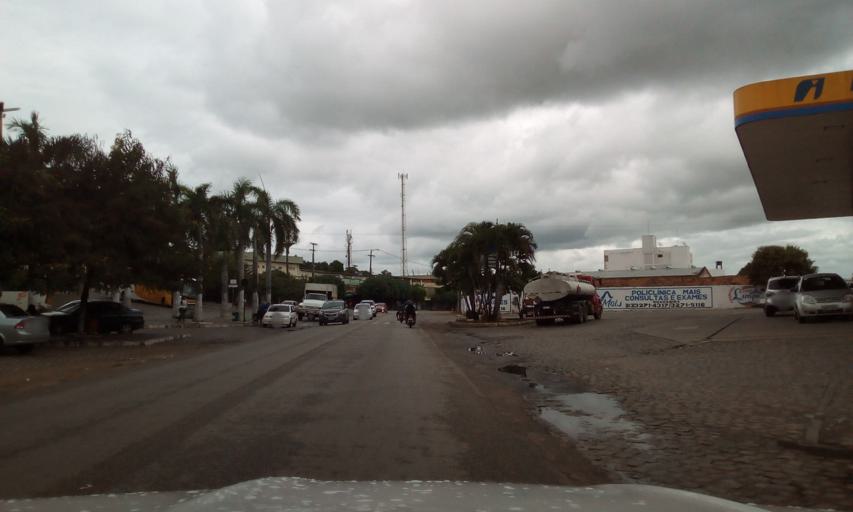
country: BR
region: Paraiba
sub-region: Guarabira
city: Guarabira
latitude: -6.8469
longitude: -35.4889
